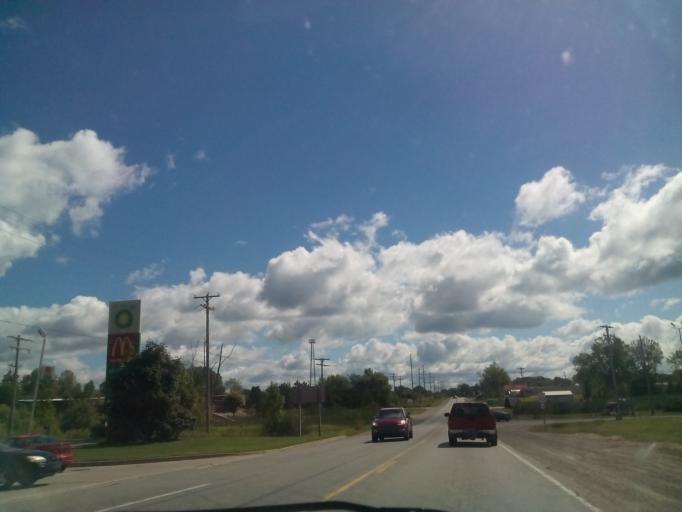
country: US
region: Michigan
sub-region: Genesee County
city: Lake Fenton
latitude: 42.8630
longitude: -83.7383
